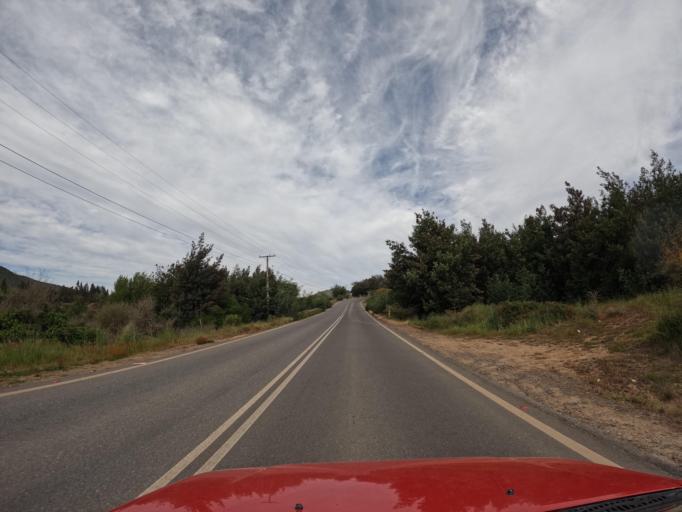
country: CL
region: Maule
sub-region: Provincia de Talca
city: Talca
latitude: -35.3232
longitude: -71.9323
